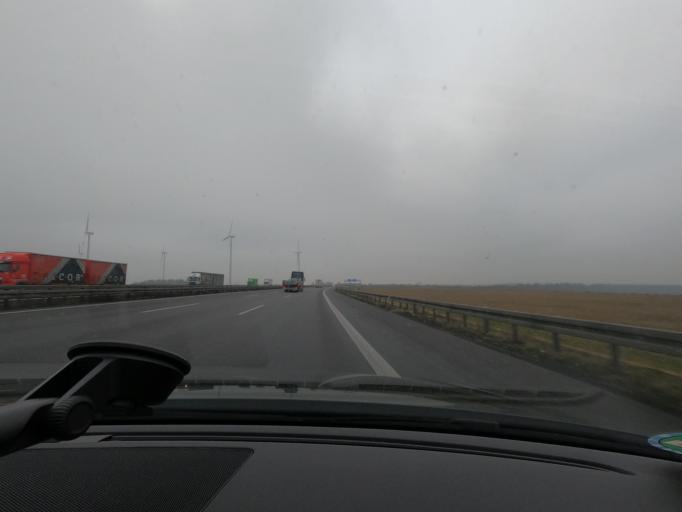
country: DE
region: North Rhine-Westphalia
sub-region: Regierungsbezirk Dusseldorf
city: Juchen
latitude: 51.0380
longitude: 6.4906
